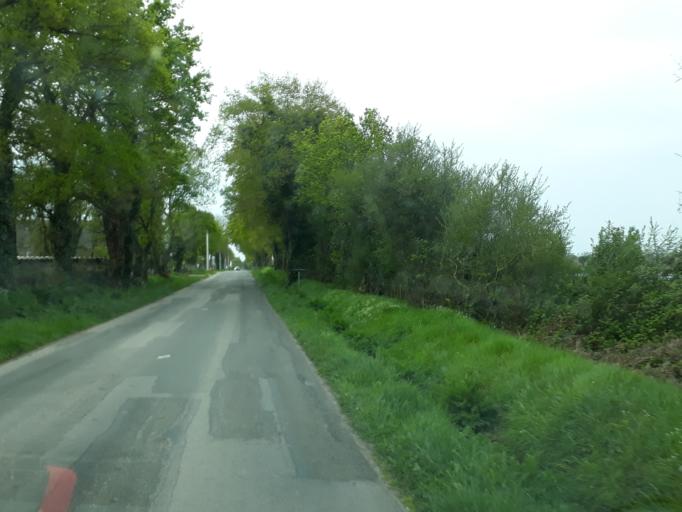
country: FR
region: Brittany
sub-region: Departement du Morbihan
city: Theix
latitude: 47.6237
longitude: -2.6759
